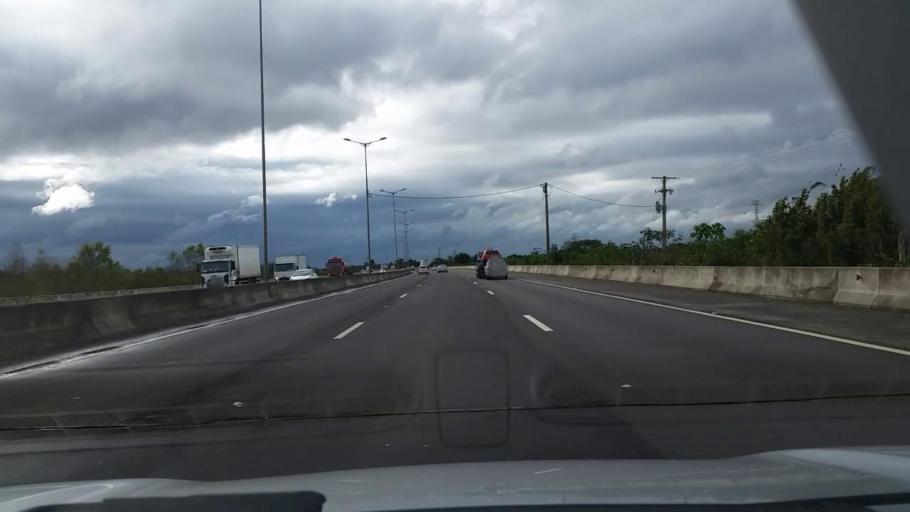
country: BR
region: Rio Grande do Sul
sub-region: Canoas
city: Canoas
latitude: -29.9442
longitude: -51.2045
